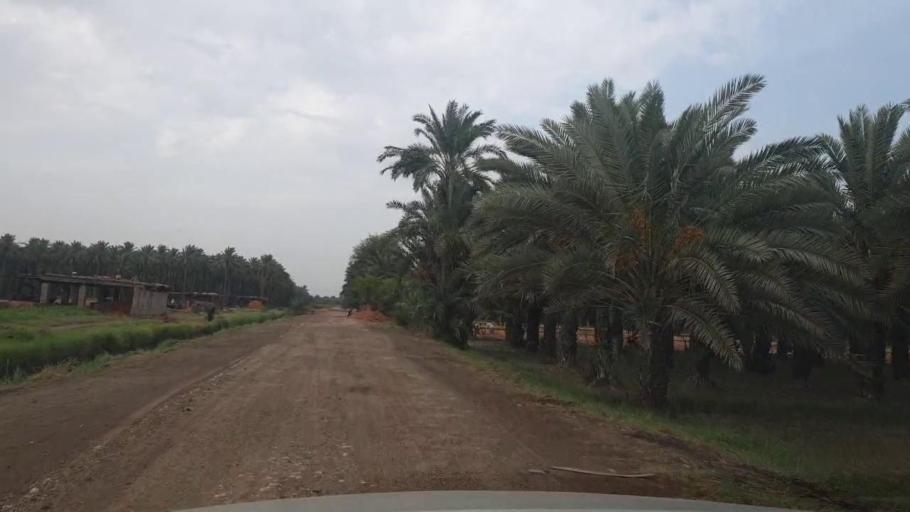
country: PK
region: Sindh
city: Sukkur
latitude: 27.6123
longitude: 68.8359
